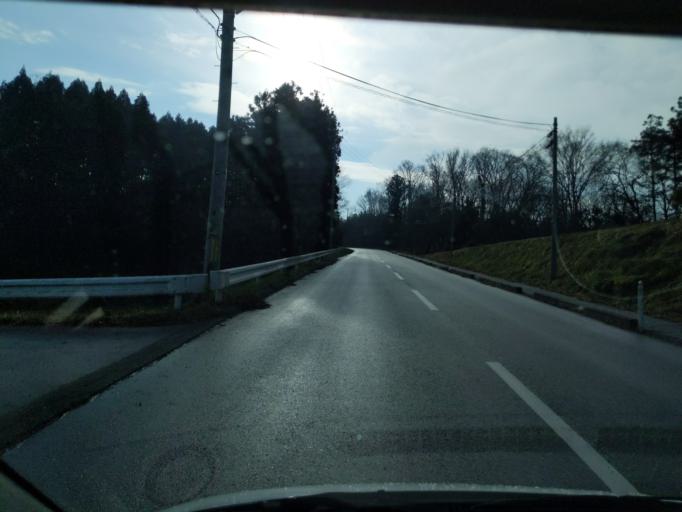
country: JP
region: Miyagi
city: Wakuya
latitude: 38.7064
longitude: 141.1589
